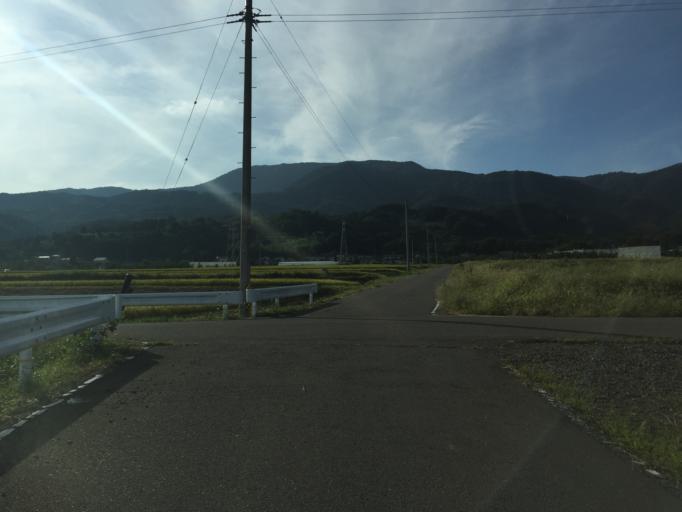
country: JP
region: Fukushima
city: Hobaramachi
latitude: 37.8809
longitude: 140.5248
